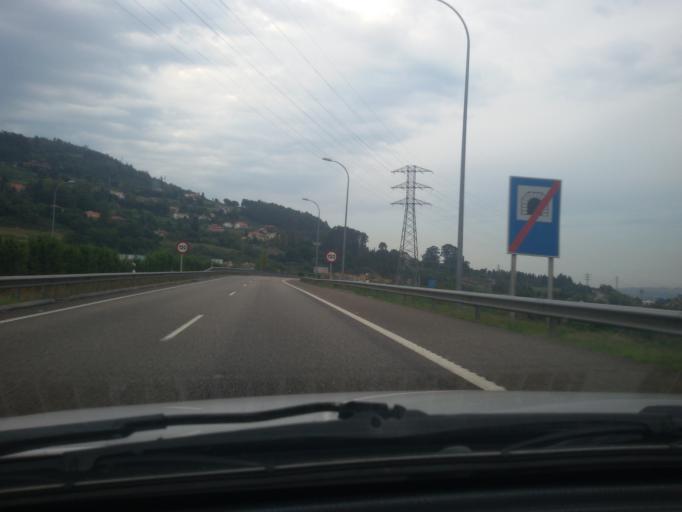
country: ES
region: Asturias
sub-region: Province of Asturias
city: Oviedo
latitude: 43.3765
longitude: -5.8416
